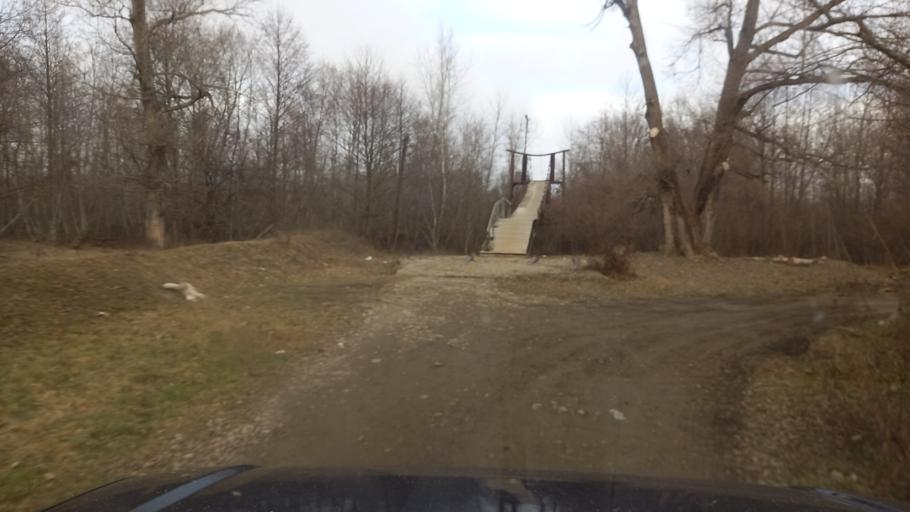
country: RU
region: Krasnodarskiy
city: Neftegorsk
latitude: 44.2435
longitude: 39.7641
